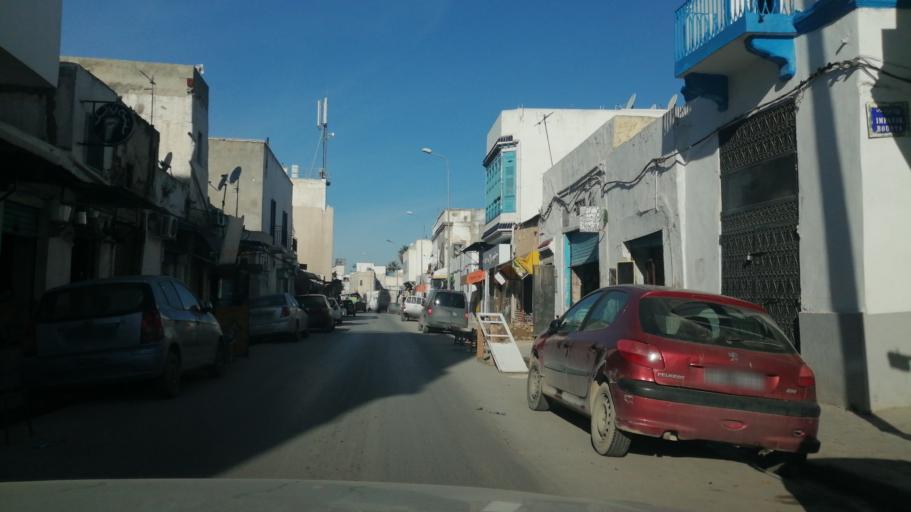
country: TN
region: Tunis
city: Tunis
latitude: 36.8061
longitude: 10.1656
